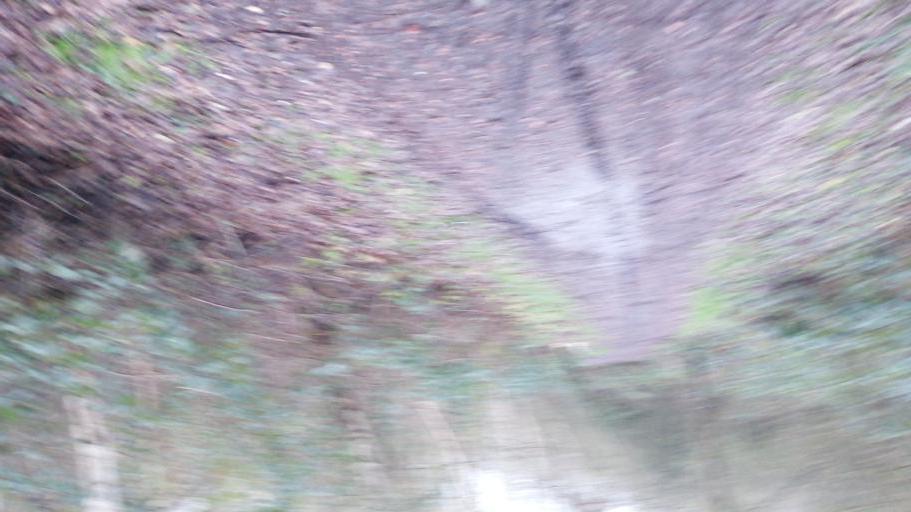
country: FR
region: Nord-Pas-de-Calais
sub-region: Departement du Pas-de-Calais
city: Billy-Montigny
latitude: 50.4073
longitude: 2.9165
